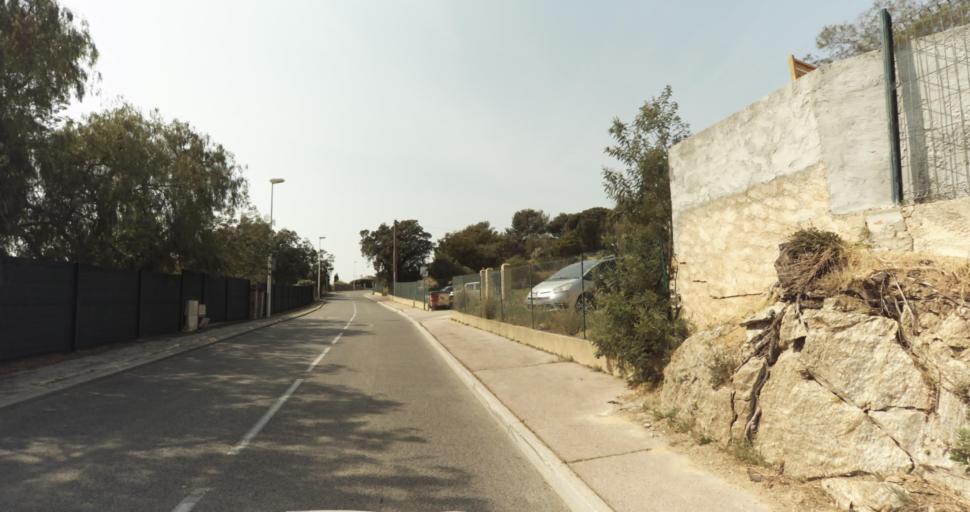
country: FR
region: Provence-Alpes-Cote d'Azur
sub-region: Departement du Var
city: Le Lavandou
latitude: 43.1408
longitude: 6.3539
